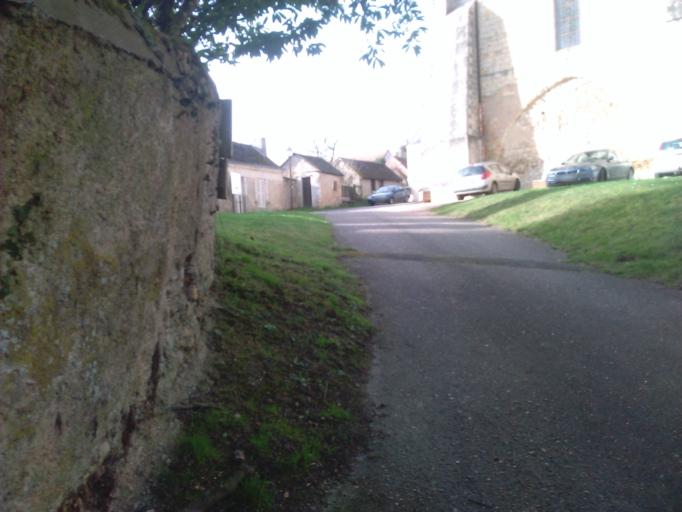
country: FR
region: Pays de la Loire
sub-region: Departement de la Sarthe
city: Besse-sur-Braye
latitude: 47.7772
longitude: 0.7929
